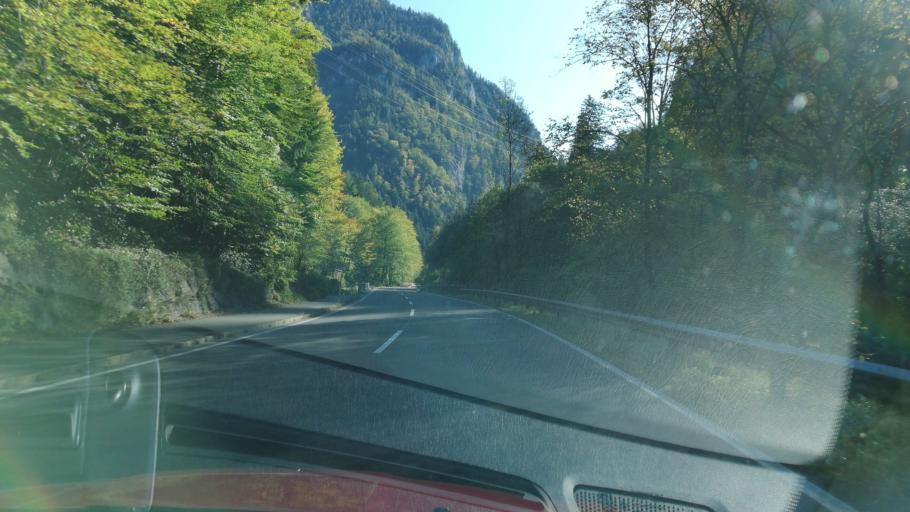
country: AT
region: Styria
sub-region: Politischer Bezirk Leoben
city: Hieflau
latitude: 47.5848
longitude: 14.8156
